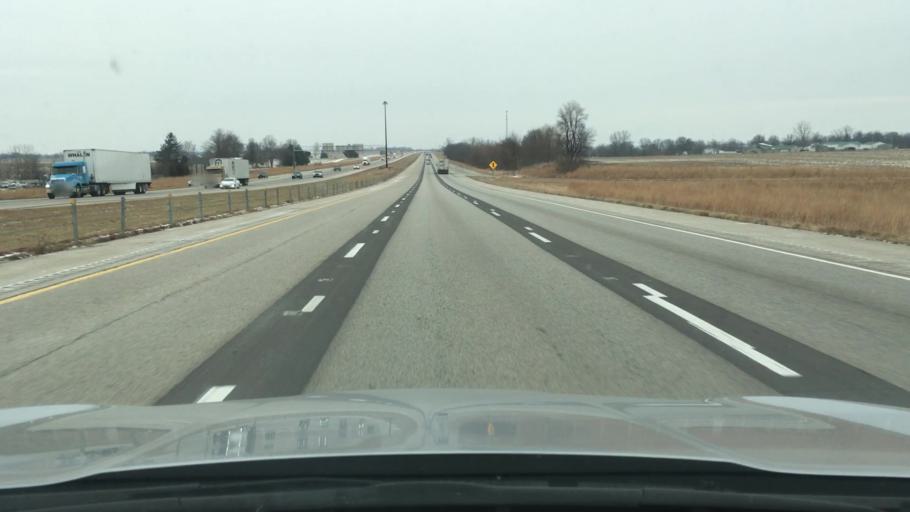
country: US
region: Illinois
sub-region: Sangamon County
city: Divernon
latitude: 39.5927
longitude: -89.6464
